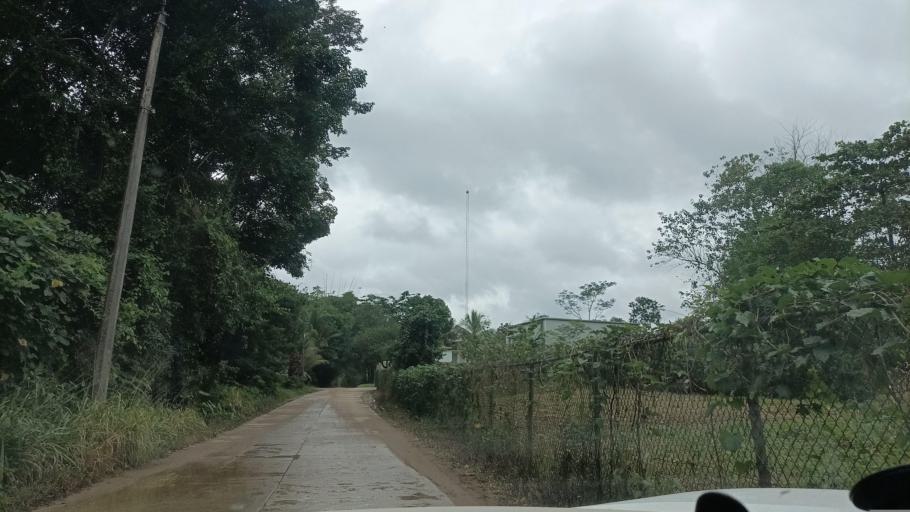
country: MX
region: Veracruz
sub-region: Uxpanapa
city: Poblado 10
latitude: 17.2765
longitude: -94.4931
